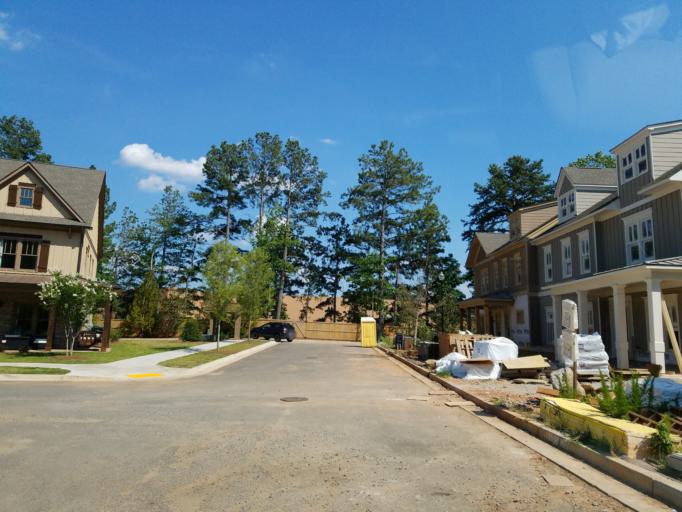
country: US
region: Georgia
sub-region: Fulton County
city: Roswell
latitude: 34.0866
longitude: -84.3580
